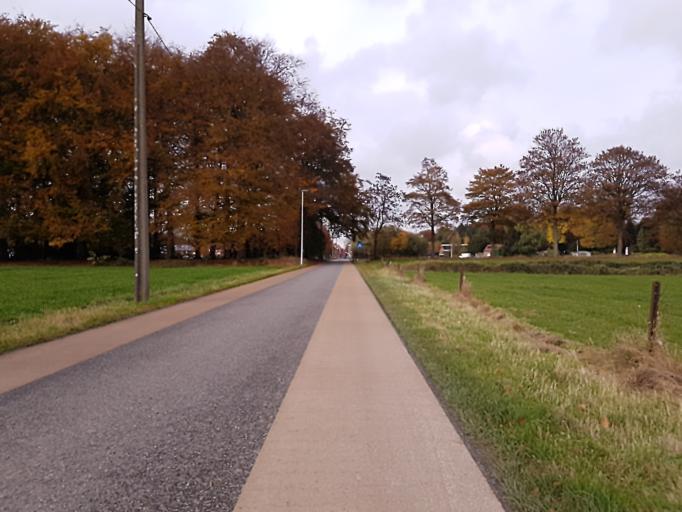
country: BE
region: Flanders
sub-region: Provincie Antwerpen
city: Boechout
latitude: 51.1569
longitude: 4.4992
